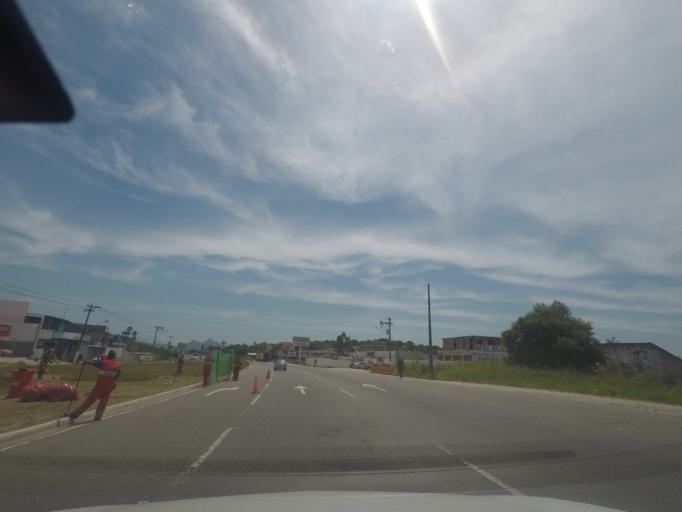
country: BR
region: Rio de Janeiro
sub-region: Marica
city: Marica
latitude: -22.9306
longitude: -42.8737
